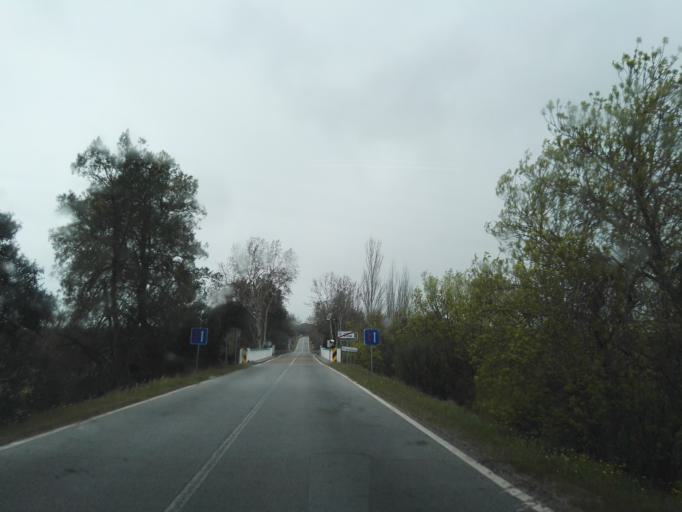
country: PT
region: Portalegre
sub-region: Arronches
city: Arronches
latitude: 39.0551
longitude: -7.2697
